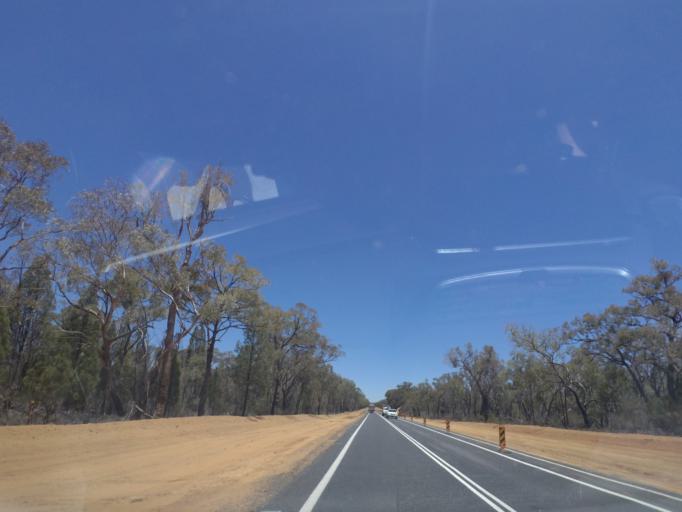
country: AU
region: New South Wales
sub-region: Warrumbungle Shire
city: Coonabarabran
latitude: -30.9278
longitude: 149.4301
